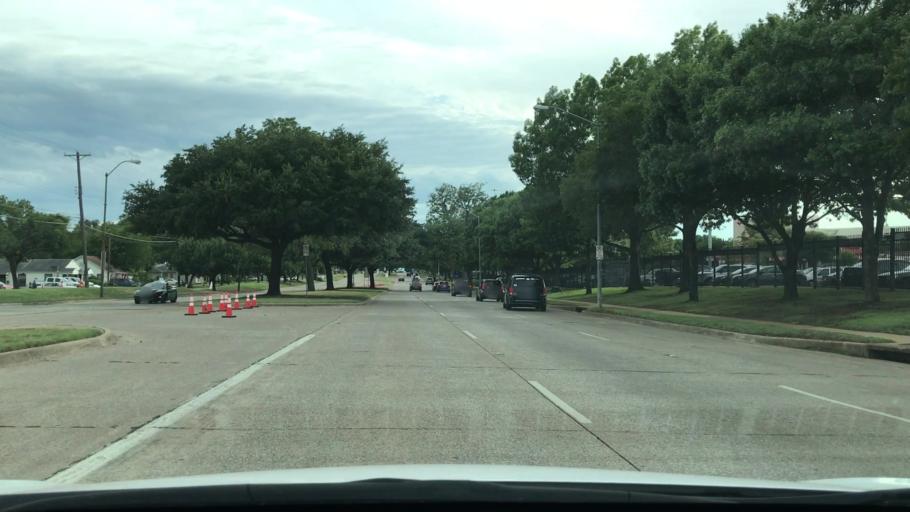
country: US
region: Texas
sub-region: Dallas County
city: Dallas
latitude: 32.7762
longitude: -96.7529
